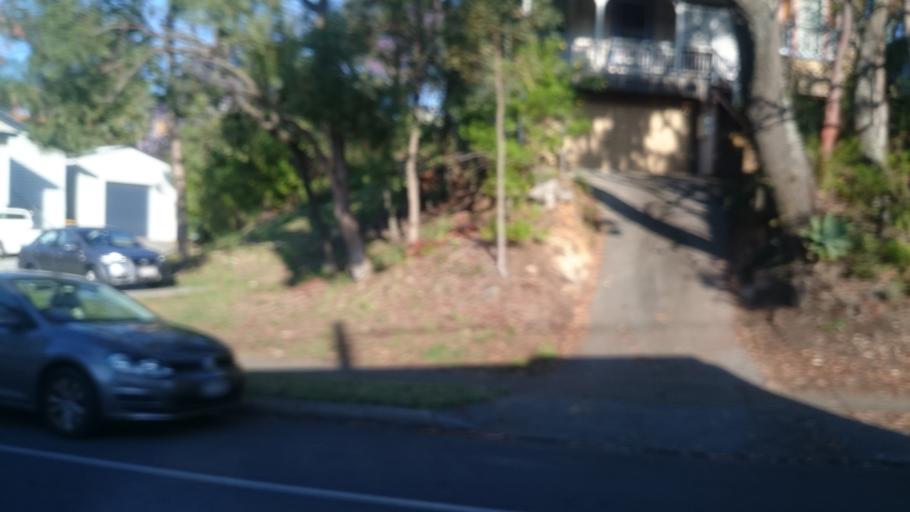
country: AU
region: Queensland
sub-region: Brisbane
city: Manly West
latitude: -27.4559
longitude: 153.1827
